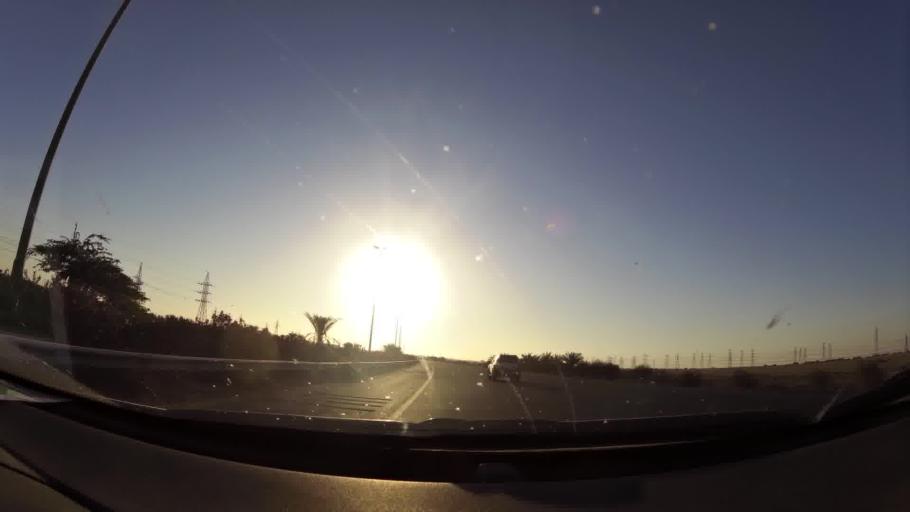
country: KW
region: Al Ahmadi
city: Al Fahahil
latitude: 28.9370
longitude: 48.1878
